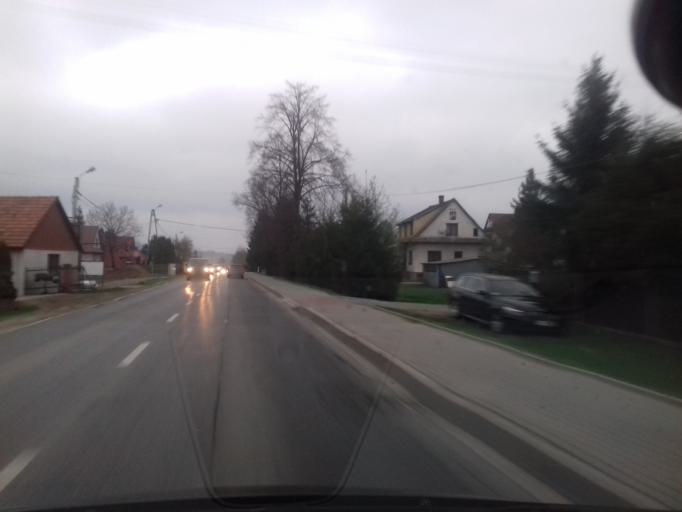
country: PL
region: Lesser Poland Voivodeship
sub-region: Powiat limanowski
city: Mszana Dolna
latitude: 49.6788
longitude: 20.0600
